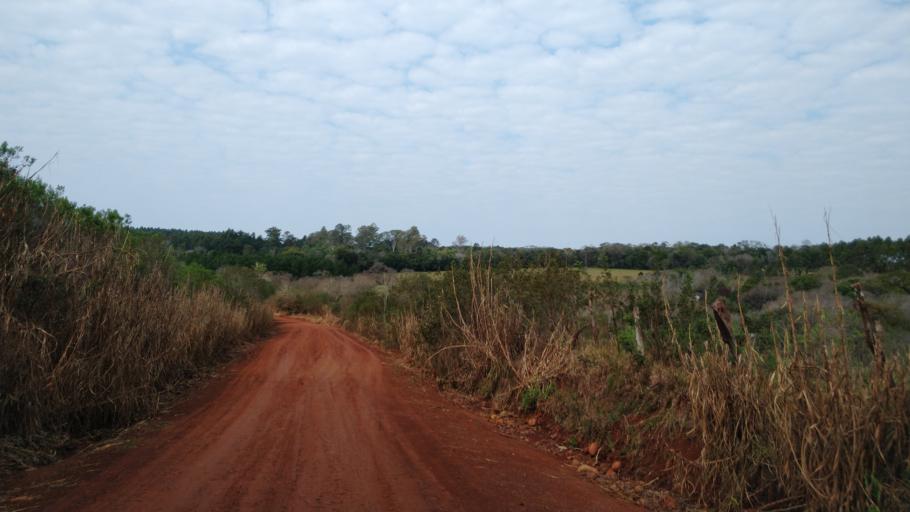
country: AR
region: Misiones
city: Capiovi
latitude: -26.9375
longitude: -55.0643
